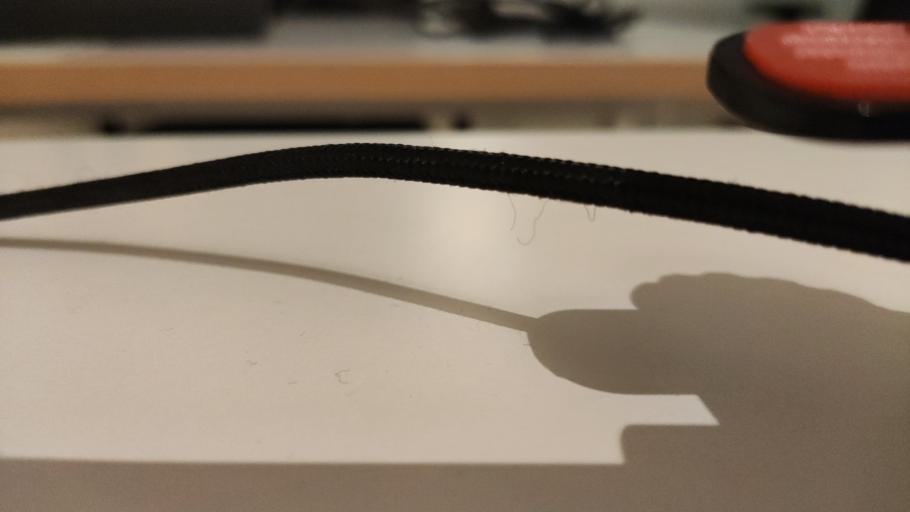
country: RU
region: Moskovskaya
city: Kurovskoye
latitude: 55.6015
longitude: 38.9259
